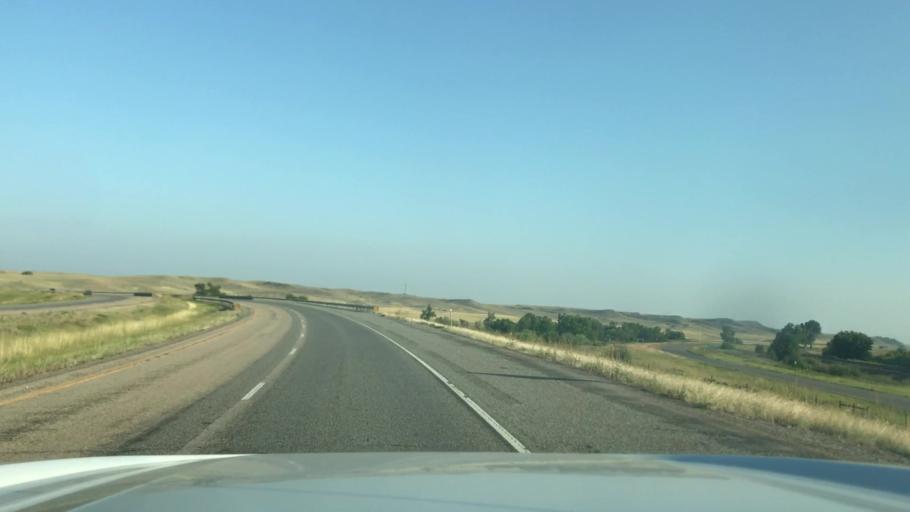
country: US
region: Montana
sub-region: Big Horn County
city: Crow Agency
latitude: 45.4922
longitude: -107.3923
